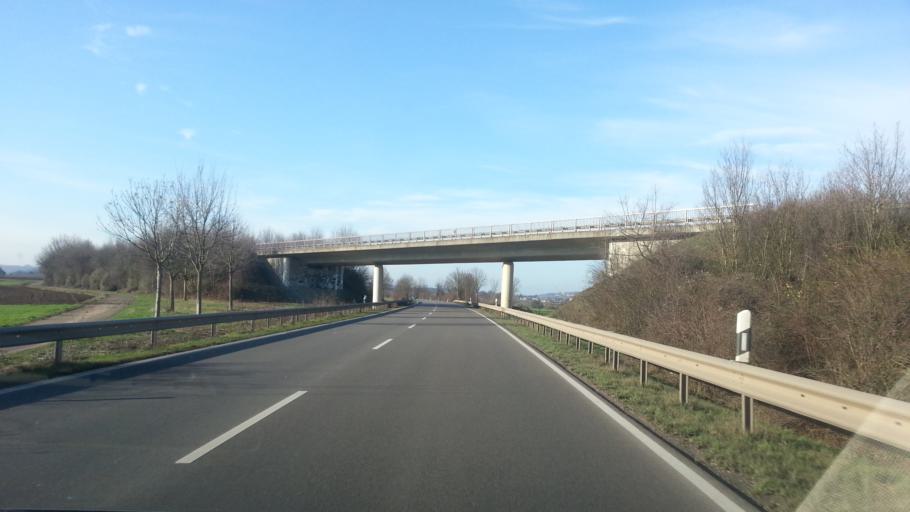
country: DE
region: Rheinland-Pfalz
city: Offstein
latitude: 49.6257
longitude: 8.2468
